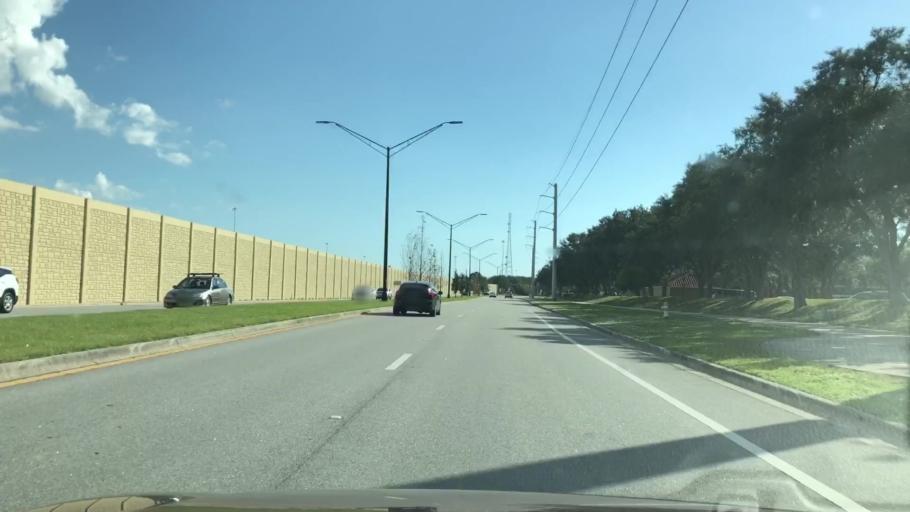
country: US
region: Florida
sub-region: Sarasota County
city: Fruitville
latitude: 27.3473
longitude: -82.4473
